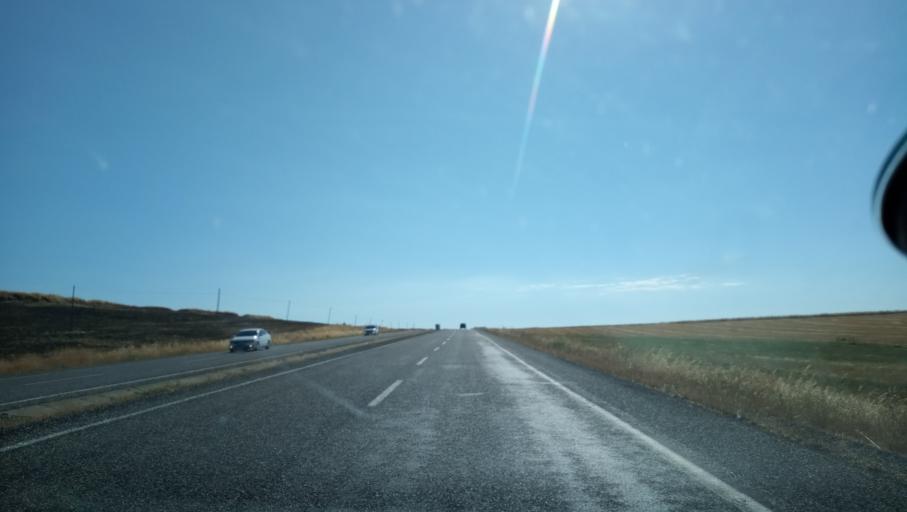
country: TR
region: Diyarbakir
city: Bagdere
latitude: 38.1296
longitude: 40.7911
